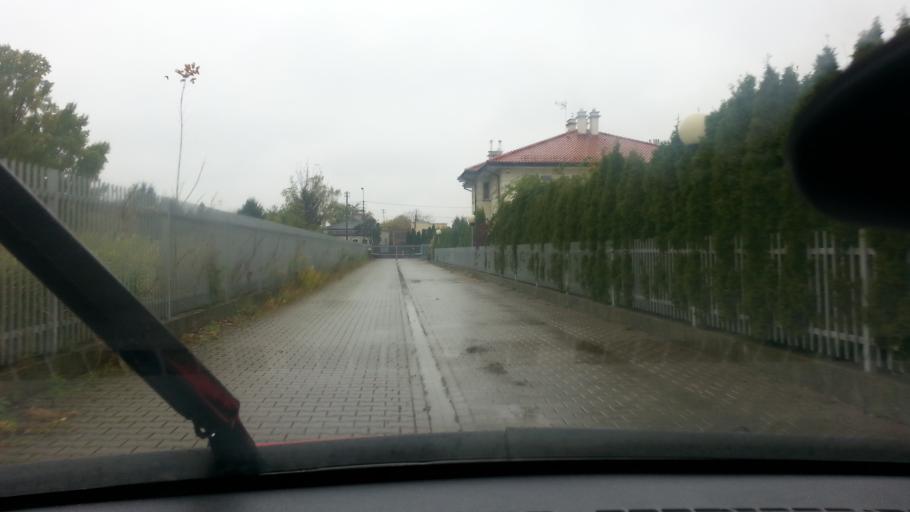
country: PL
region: Masovian Voivodeship
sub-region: Powiat pruszkowski
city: Michalowice
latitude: 52.1721
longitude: 20.8629
